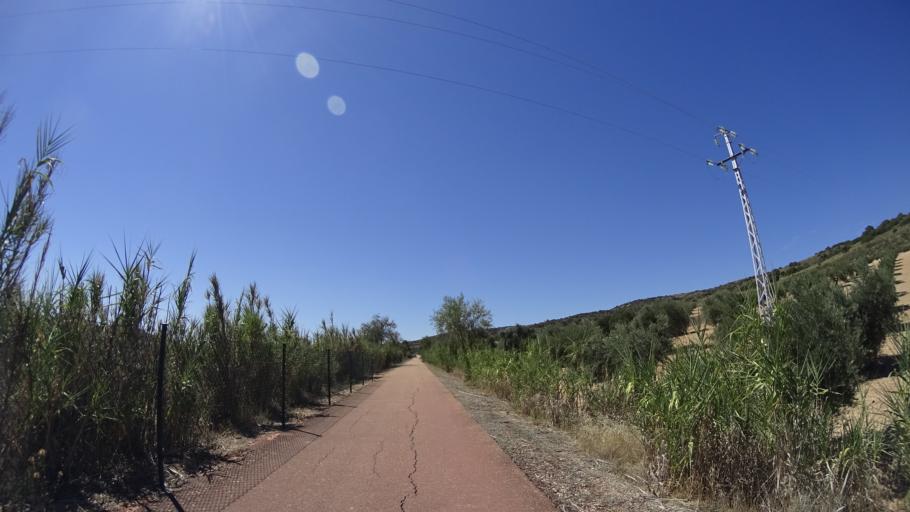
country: ES
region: Madrid
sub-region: Provincia de Madrid
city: Perales de Tajuna
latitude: 40.2308
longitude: -3.3780
